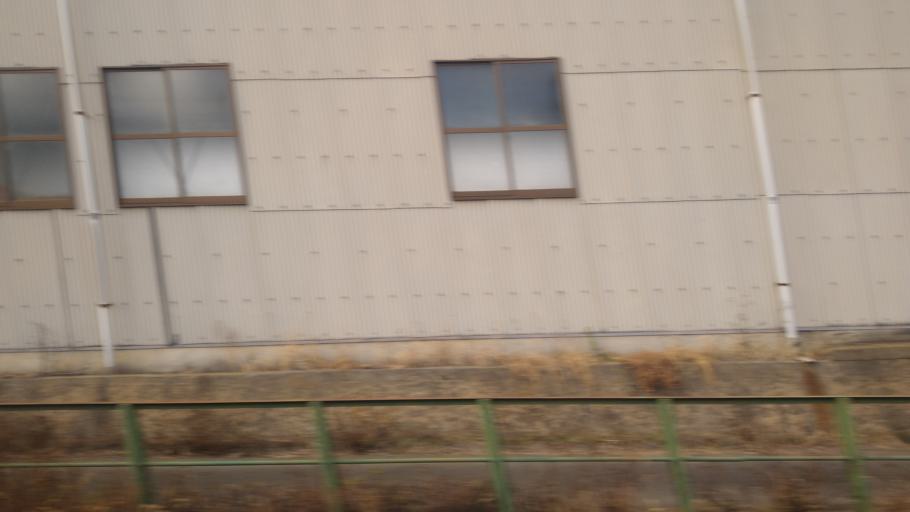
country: JP
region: Nagano
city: Shiojiri
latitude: 36.0932
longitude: 137.9241
